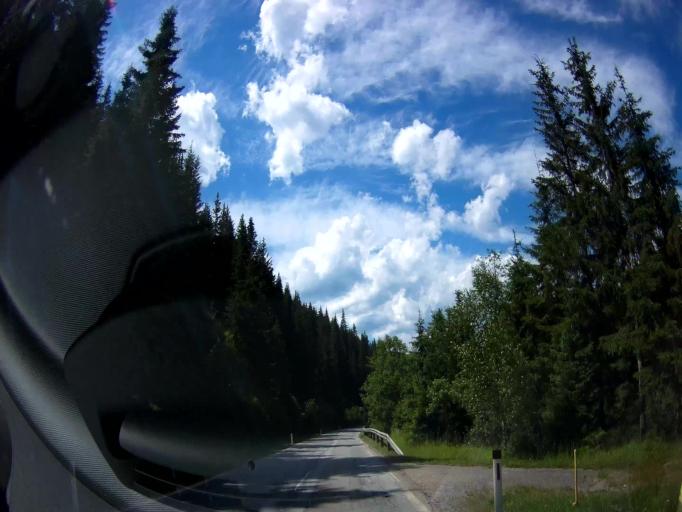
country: AT
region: Styria
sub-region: Politischer Bezirk Murau
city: Stadl an der Mur
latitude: 47.0019
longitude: 14.0127
